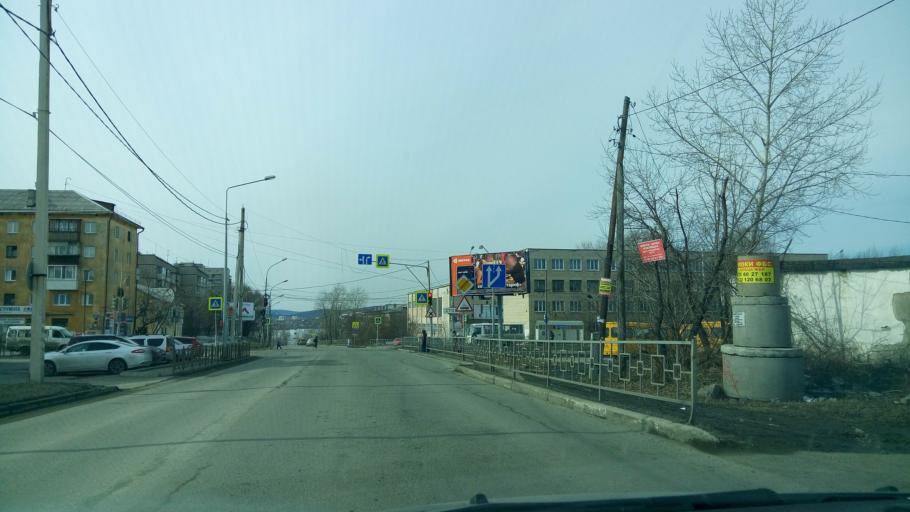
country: RU
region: Sverdlovsk
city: Nizhniy Tagil
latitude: 57.9056
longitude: 59.9961
